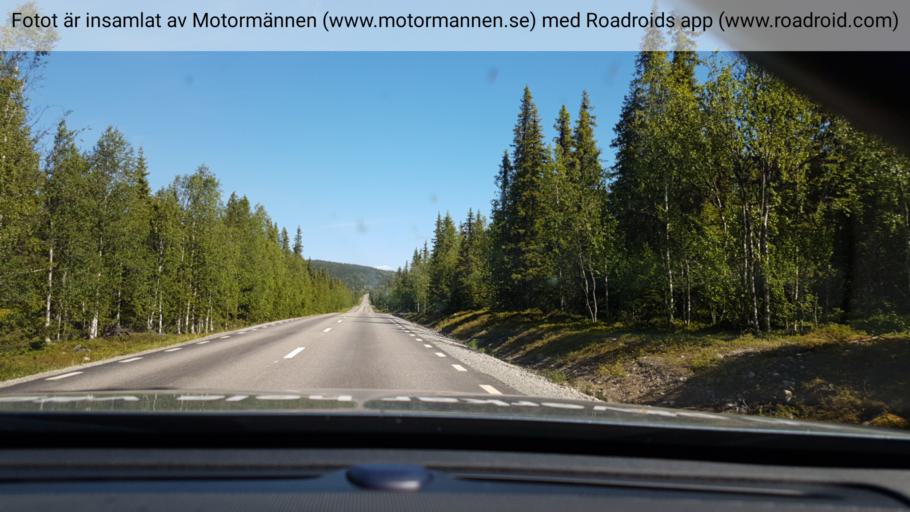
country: SE
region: Vaesterbotten
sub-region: Asele Kommun
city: Insjon
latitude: 64.7231
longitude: 17.6198
